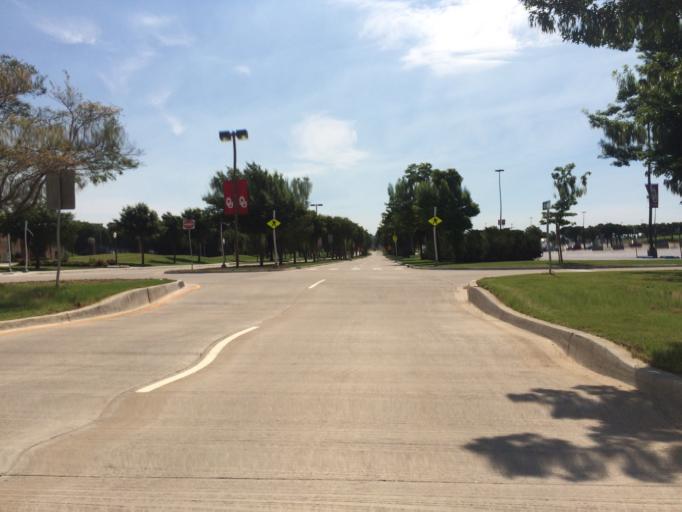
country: US
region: Oklahoma
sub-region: Cleveland County
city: Norman
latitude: 35.1894
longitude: -97.4474
